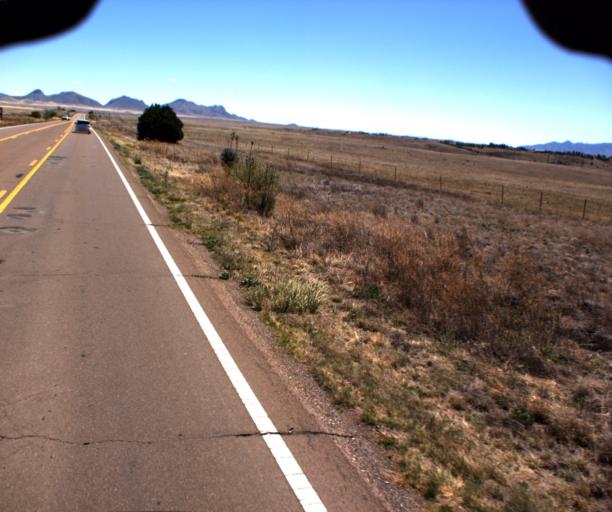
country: US
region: Arizona
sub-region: Pima County
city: Corona de Tucson
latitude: 31.6804
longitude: -110.6474
